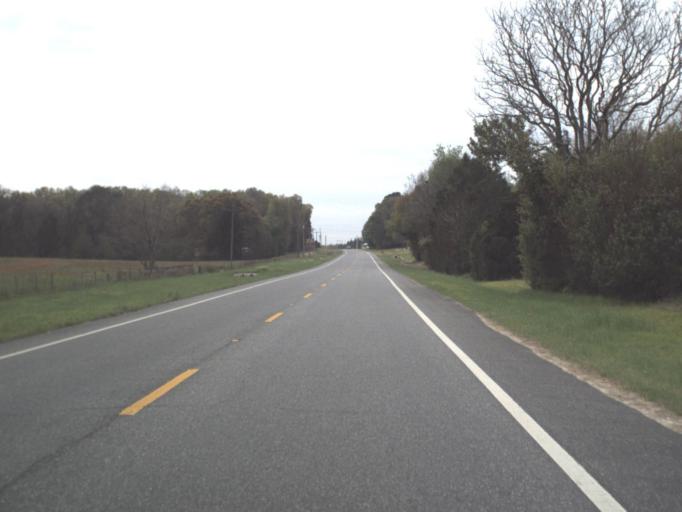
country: US
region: Florida
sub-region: Calhoun County
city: Blountstown
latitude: 30.5413
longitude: -85.1903
